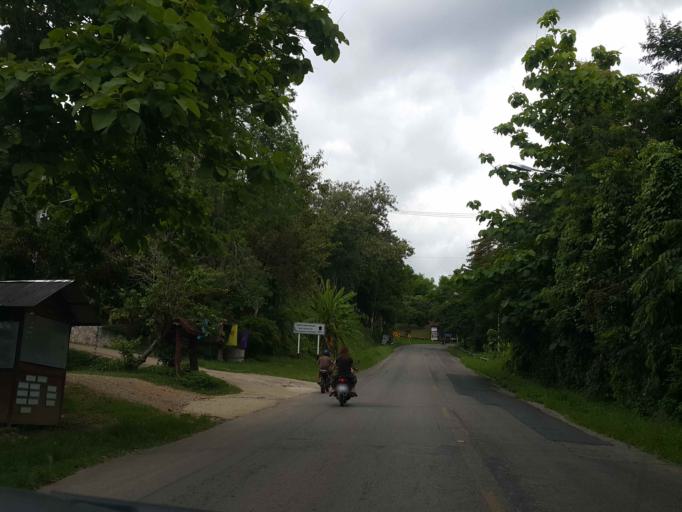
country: TH
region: Chiang Mai
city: Hang Dong
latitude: 18.7853
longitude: 98.8431
